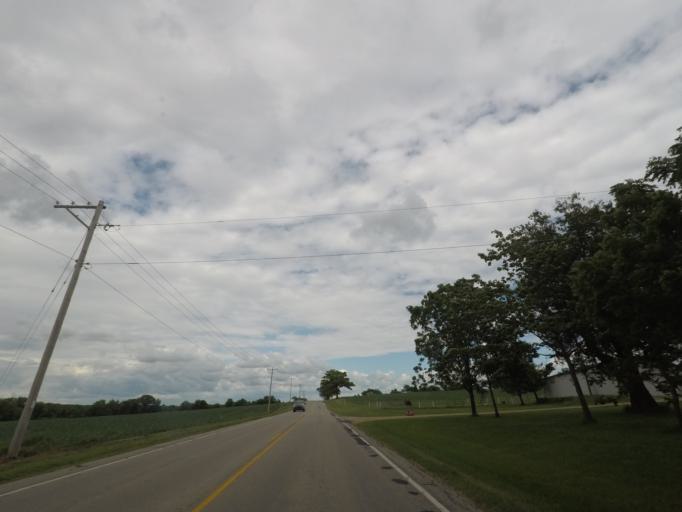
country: US
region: Wisconsin
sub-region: Green County
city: Brooklyn
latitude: 42.8478
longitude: -89.3988
